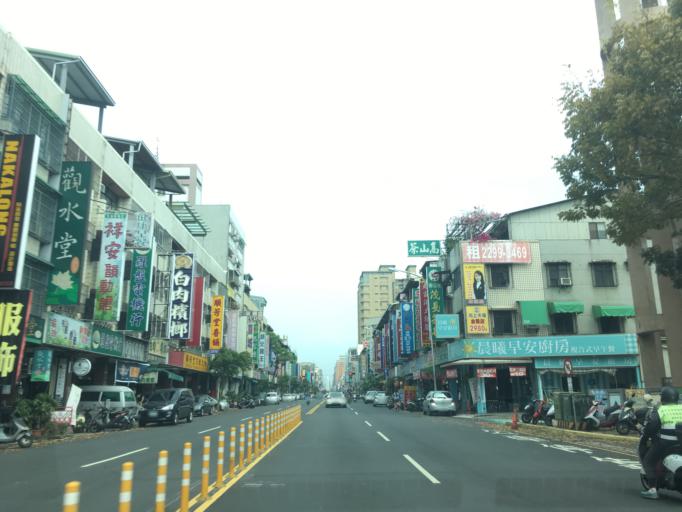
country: TW
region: Taiwan
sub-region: Taichung City
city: Taichung
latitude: 24.1668
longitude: 120.6662
